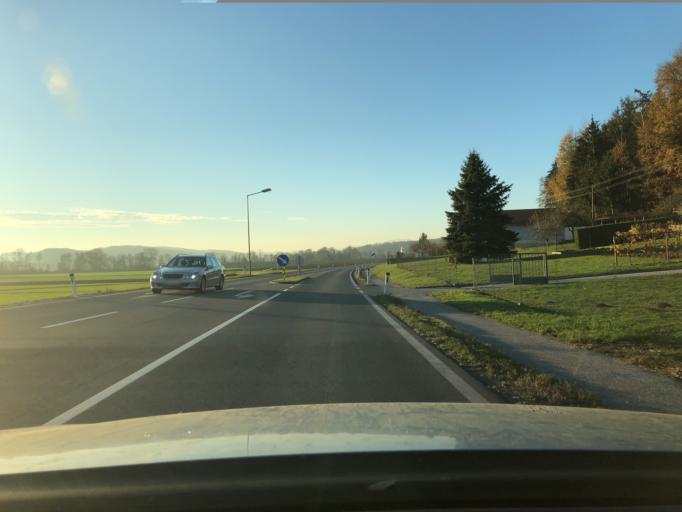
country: AT
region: Styria
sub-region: Politischer Bezirk Hartberg-Fuerstenfeld
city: Nestelbach im Ilztal
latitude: 47.0945
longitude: 15.8645
